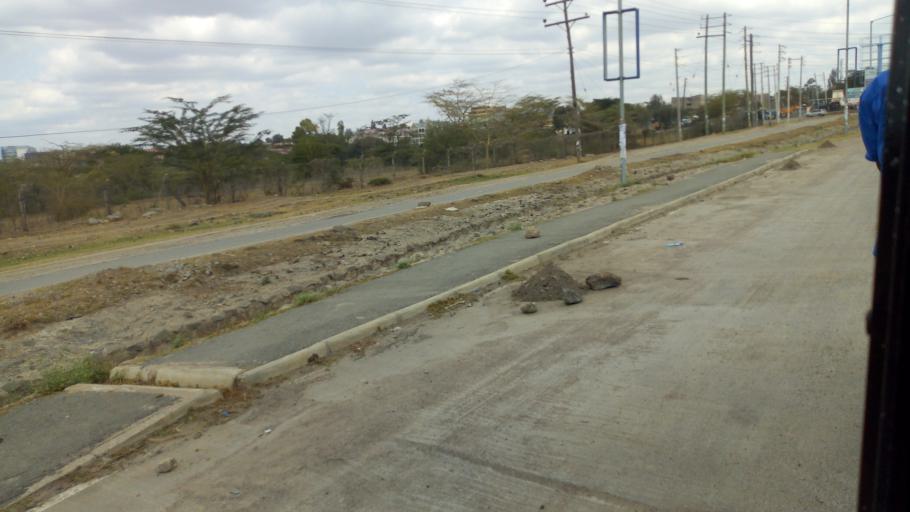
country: KE
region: Machakos
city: Athi River
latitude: -1.4673
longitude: 36.9614
